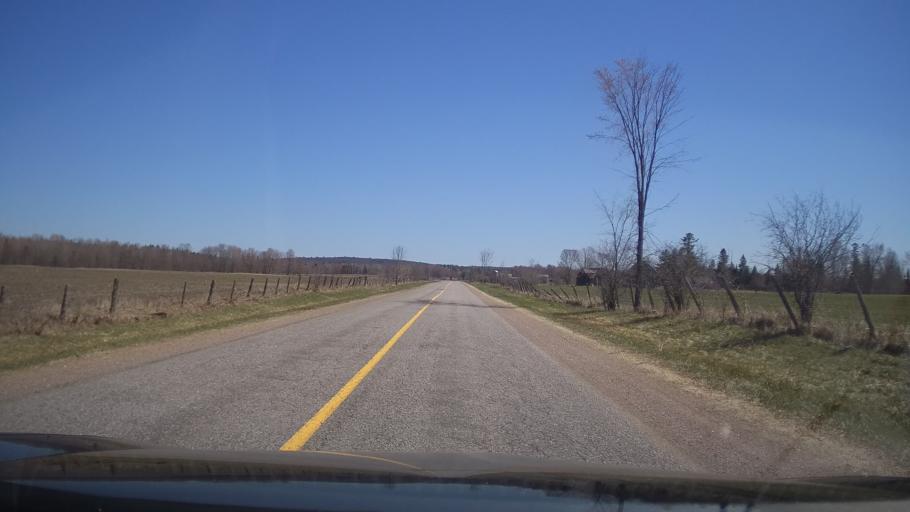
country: CA
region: Quebec
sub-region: Outaouais
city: Shawville
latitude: 45.5451
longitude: -76.3890
